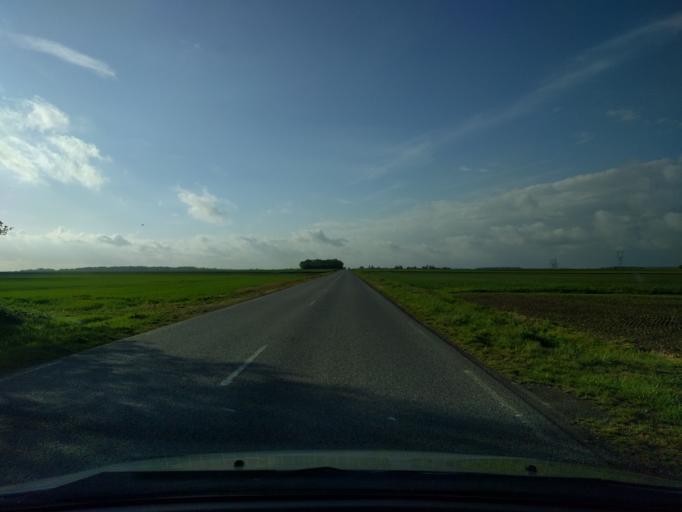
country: FR
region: Haute-Normandie
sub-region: Departement de l'Eure
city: Damville
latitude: 48.8977
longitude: 1.0356
